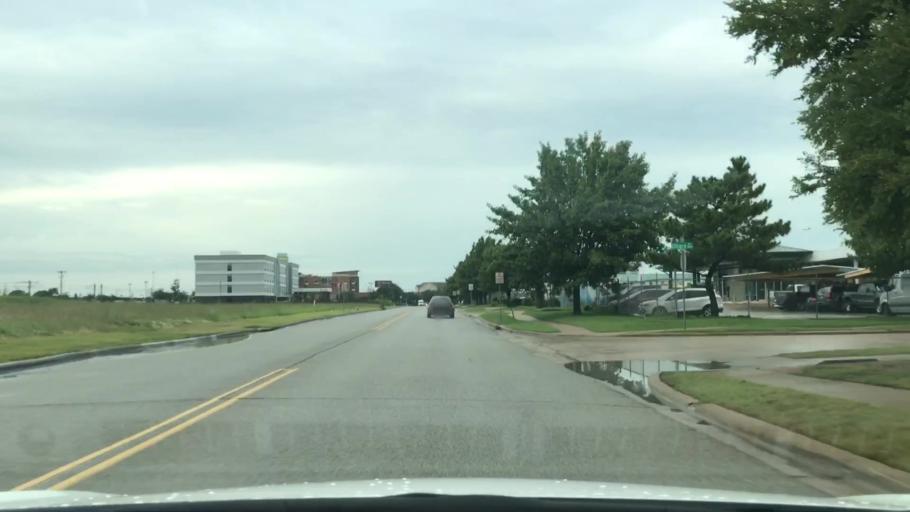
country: US
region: Texas
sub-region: Dallas County
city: Coppell
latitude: 32.9131
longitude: -97.0115
